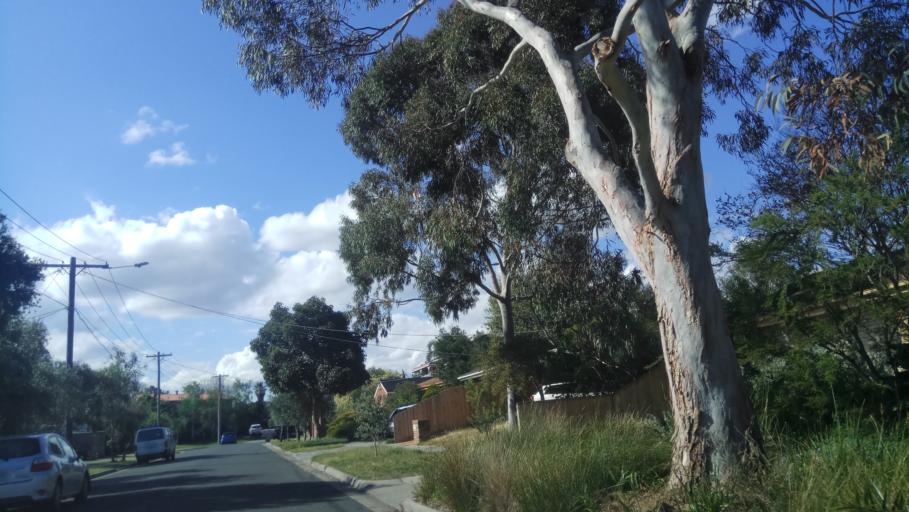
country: AU
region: Victoria
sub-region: Kingston
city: Dingley Village
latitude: -37.9878
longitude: 145.1328
